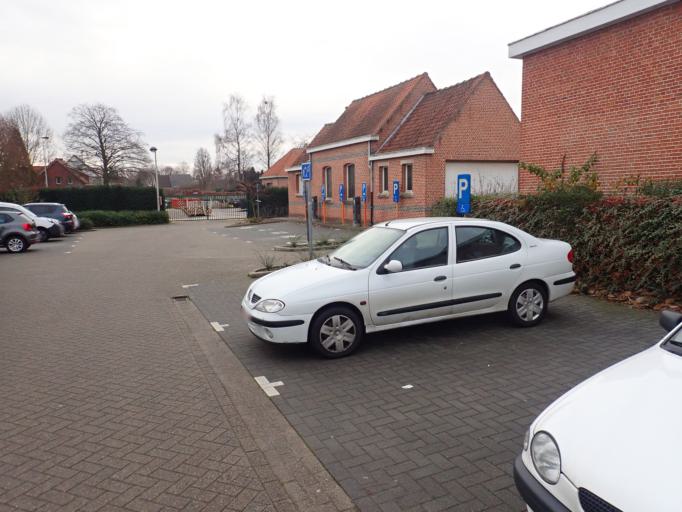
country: BE
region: Flanders
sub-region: Provincie Antwerpen
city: Wijnegem
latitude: 51.2259
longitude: 4.5147
